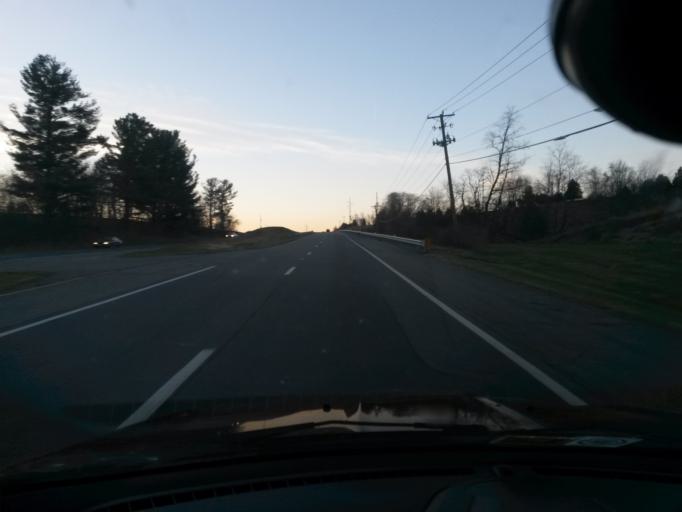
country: US
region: Virginia
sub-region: Botetourt County
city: Daleville
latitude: 37.4346
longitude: -79.9037
